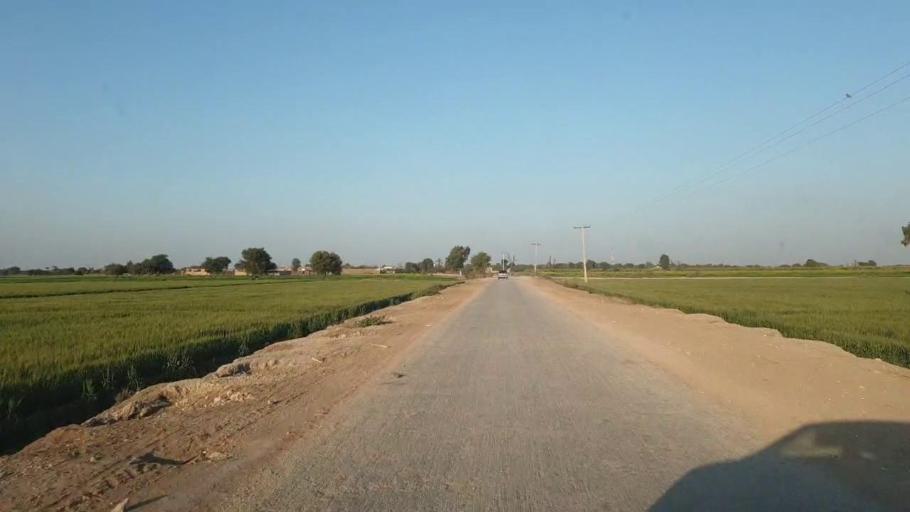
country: PK
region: Sindh
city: Tando Allahyar
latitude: 25.3837
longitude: 68.7537
